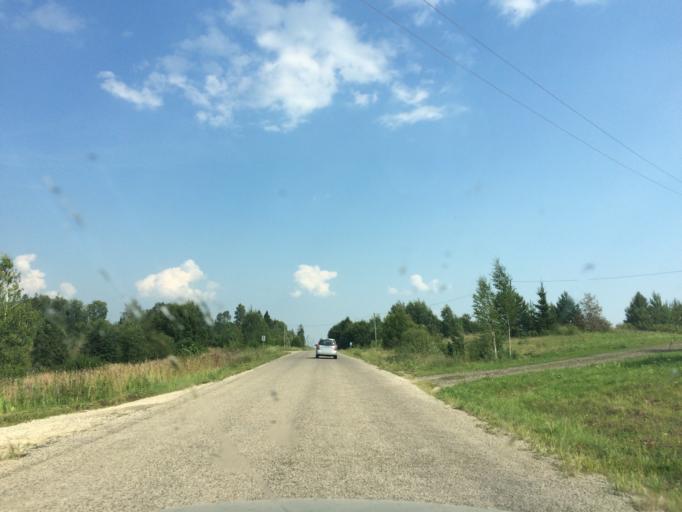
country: LV
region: Rezekne
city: Rezekne
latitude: 56.5582
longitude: 27.4199
